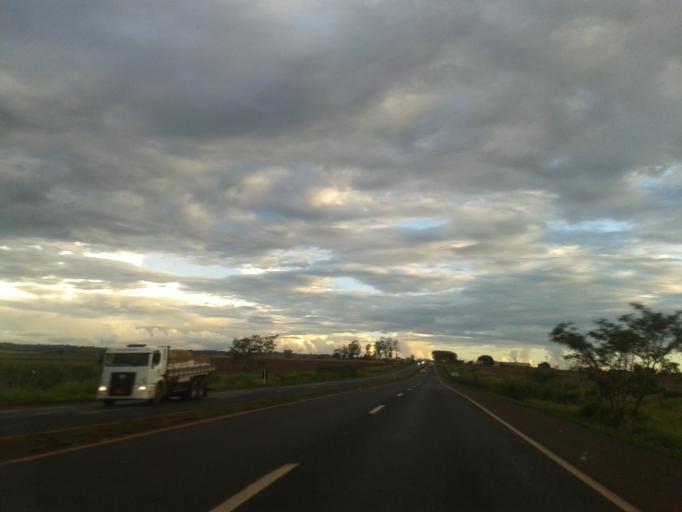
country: BR
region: Minas Gerais
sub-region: Centralina
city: Centralina
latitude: -18.5586
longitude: -49.1939
